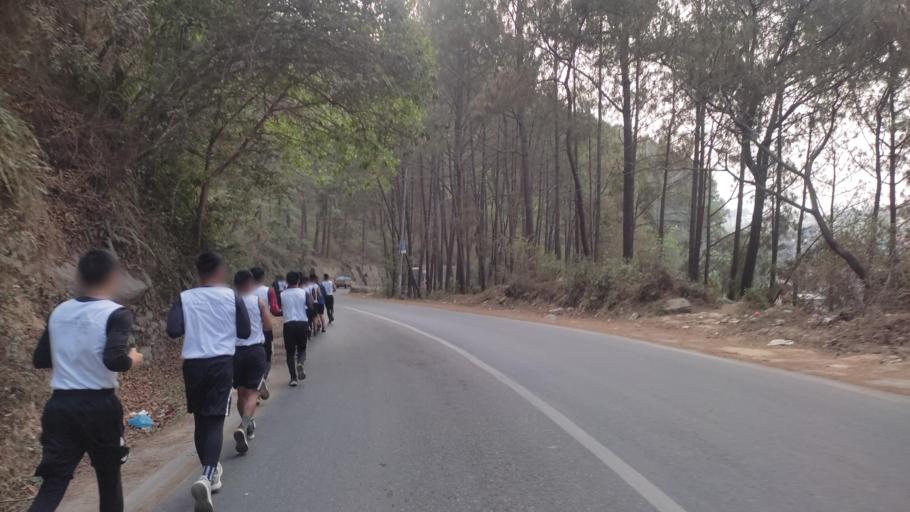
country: NP
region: Central Region
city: Kirtipur
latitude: 27.6689
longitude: 85.2924
